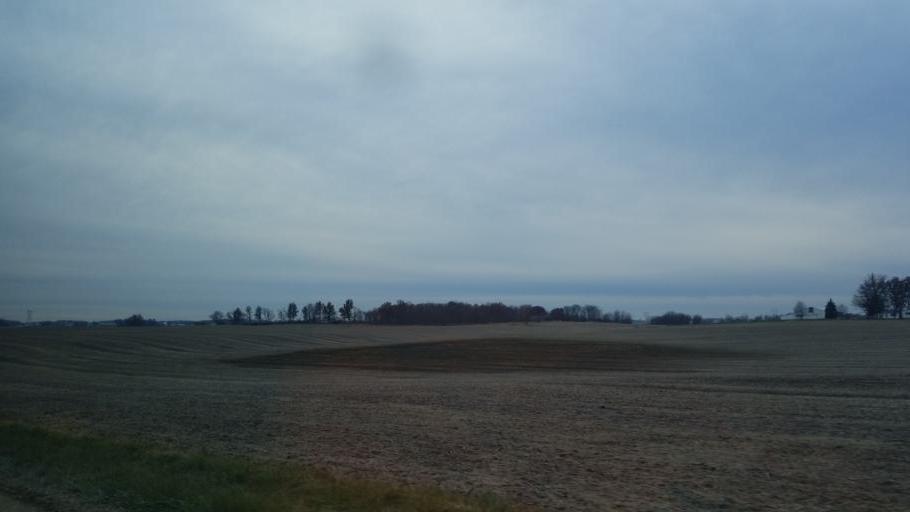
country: US
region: Indiana
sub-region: Adams County
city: Berne
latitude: 40.6794
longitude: -84.8789
